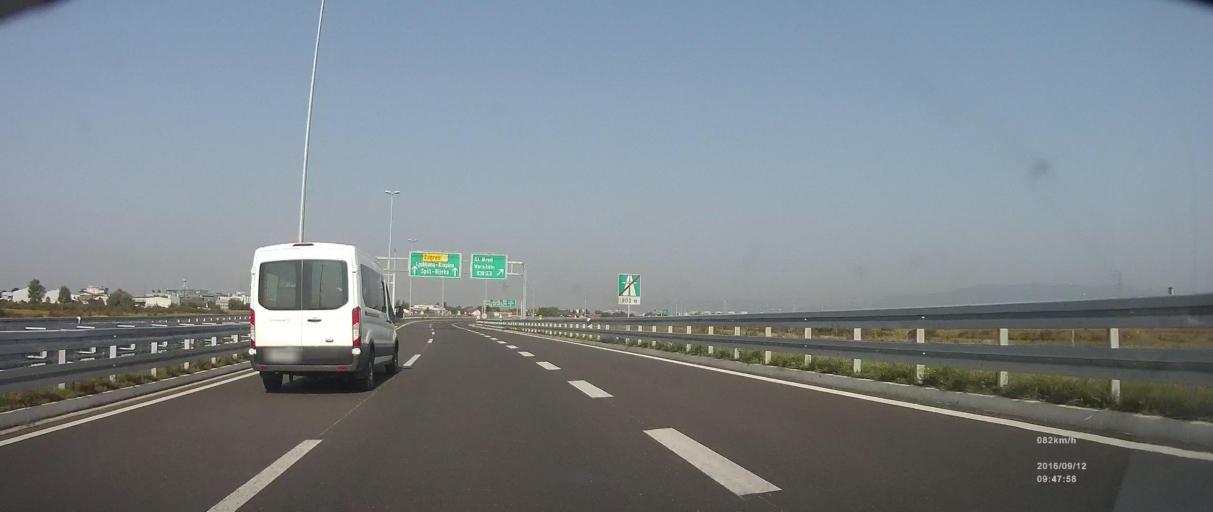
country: HR
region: Grad Zagreb
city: Odra
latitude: 45.7457
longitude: 16.0085
